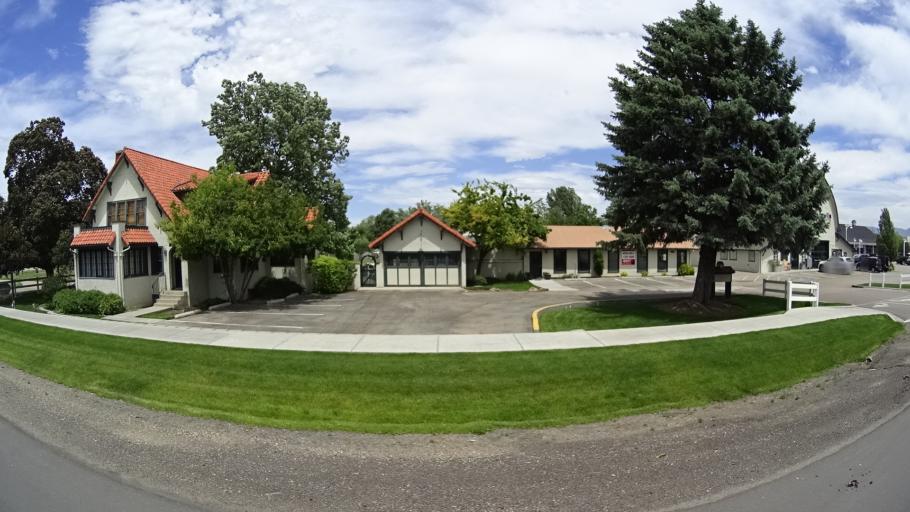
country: US
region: Idaho
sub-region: Ada County
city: Meridian
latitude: 43.6195
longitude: -116.3402
